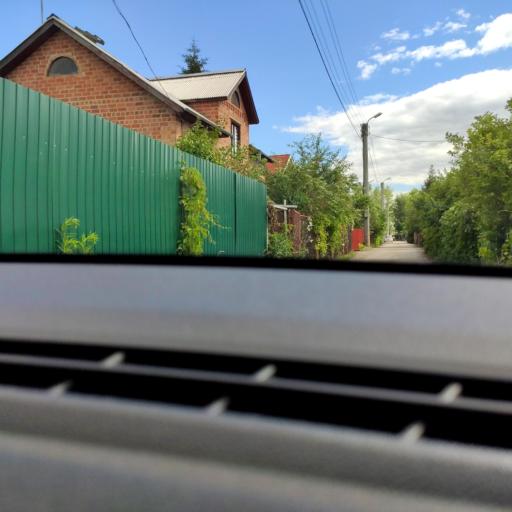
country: RU
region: Samara
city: Podstepki
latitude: 53.5816
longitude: 49.0676
